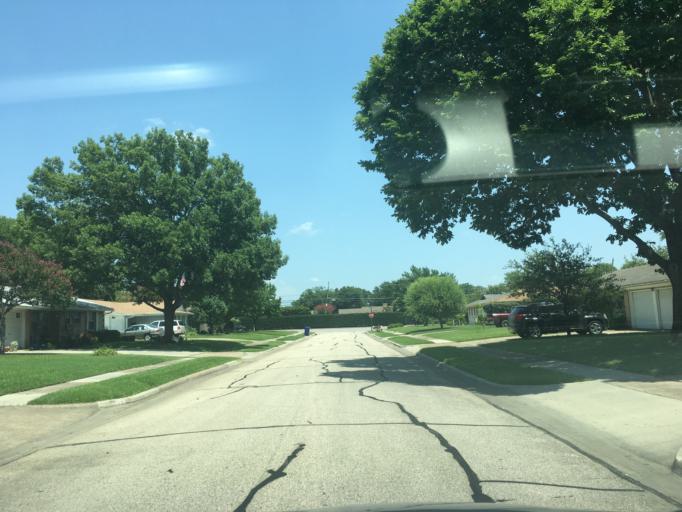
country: US
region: Texas
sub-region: Dallas County
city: Carrollton
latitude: 32.9380
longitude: -96.8749
